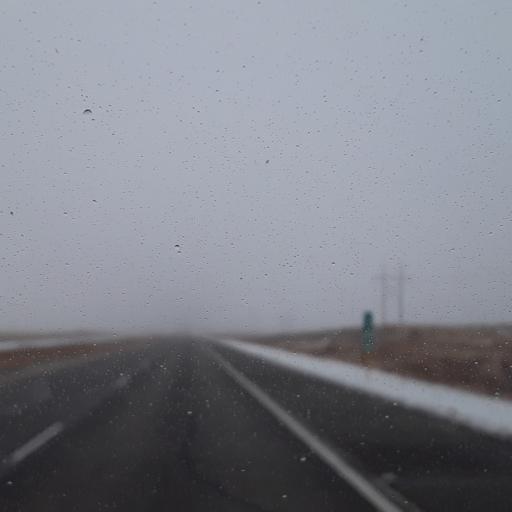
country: US
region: Colorado
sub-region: Logan County
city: Sterling
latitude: 40.7775
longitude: -102.9217
